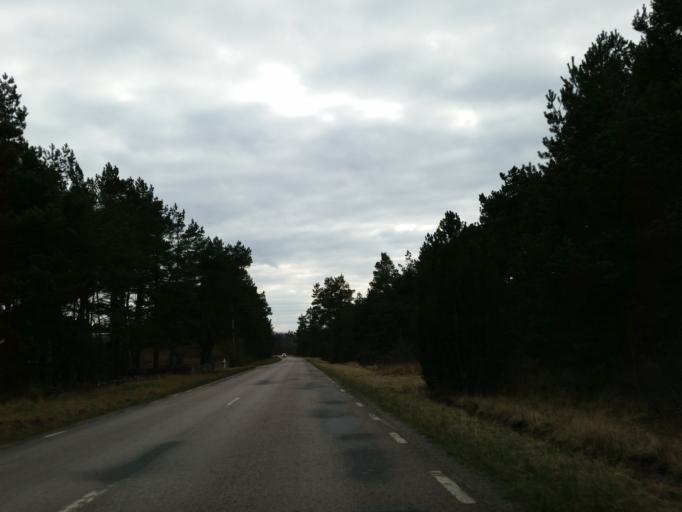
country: SE
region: Kalmar
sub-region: Morbylanga Kommun
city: Sodra Sandby
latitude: 56.5822
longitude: 16.6223
